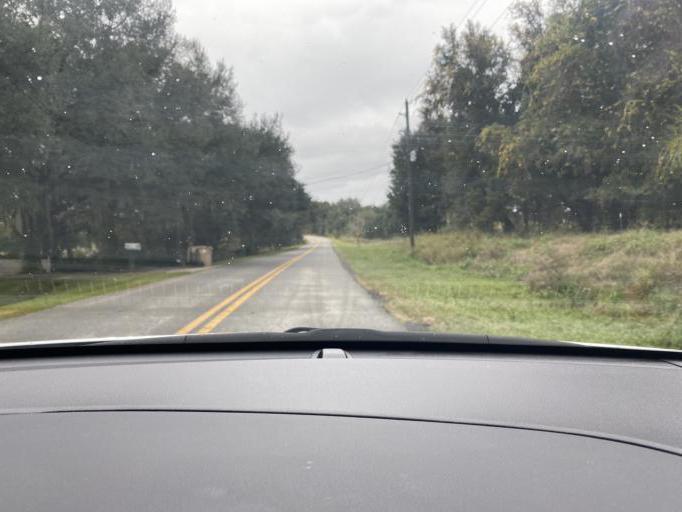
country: US
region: Florida
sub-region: Lake County
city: Groveland
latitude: 28.6058
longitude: -81.8138
